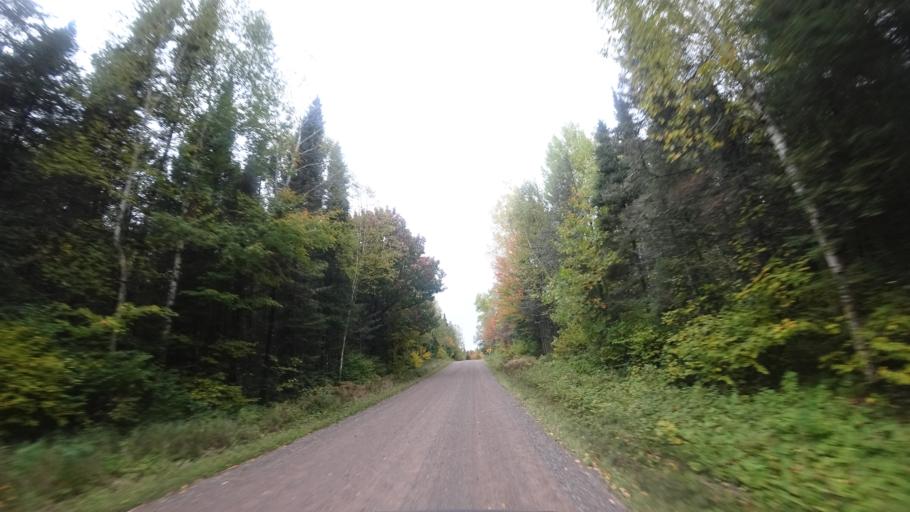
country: US
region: Wisconsin
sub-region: Sawyer County
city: Little Round Lake
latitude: 46.0773
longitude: -90.9929
